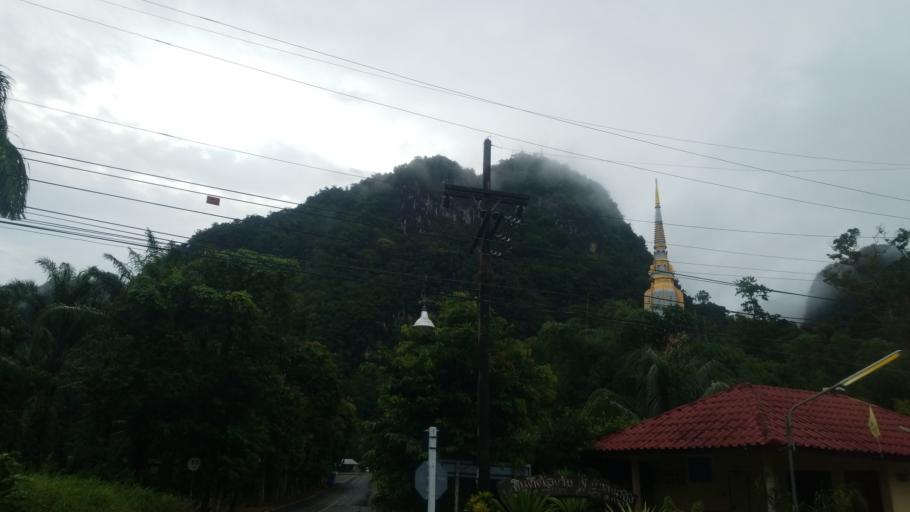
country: TH
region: Krabi
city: Krabi
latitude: 8.1226
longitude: 98.9269
